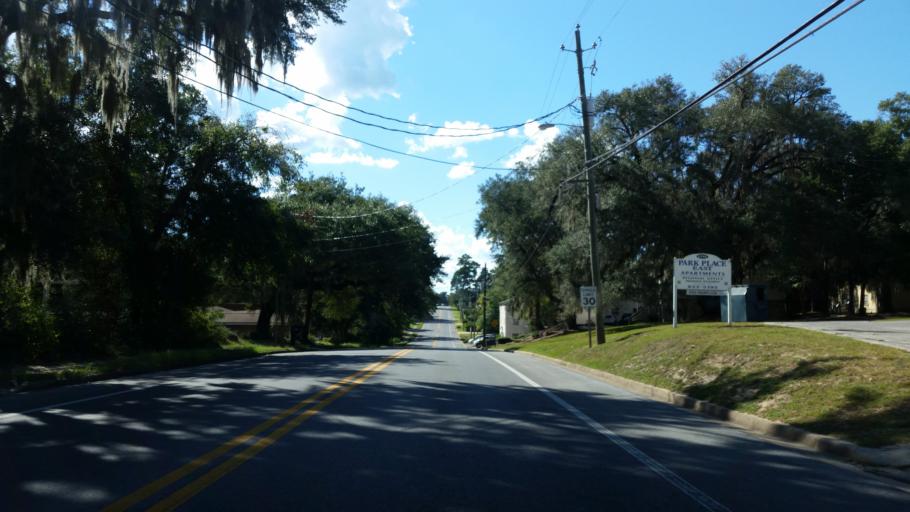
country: US
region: Florida
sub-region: Santa Rosa County
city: Milton
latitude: 30.6309
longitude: -87.0477
